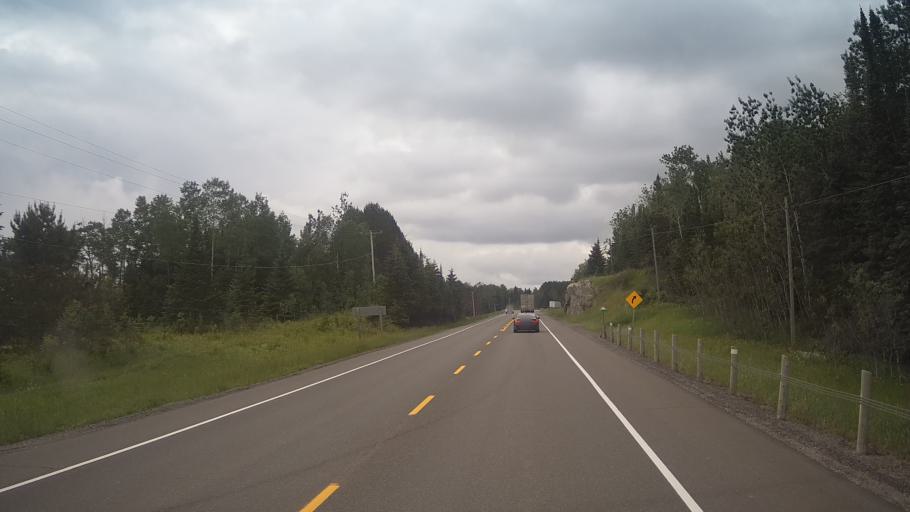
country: CA
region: Ontario
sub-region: Thunder Bay District
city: Thunder Bay
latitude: 48.5136
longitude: -89.4923
